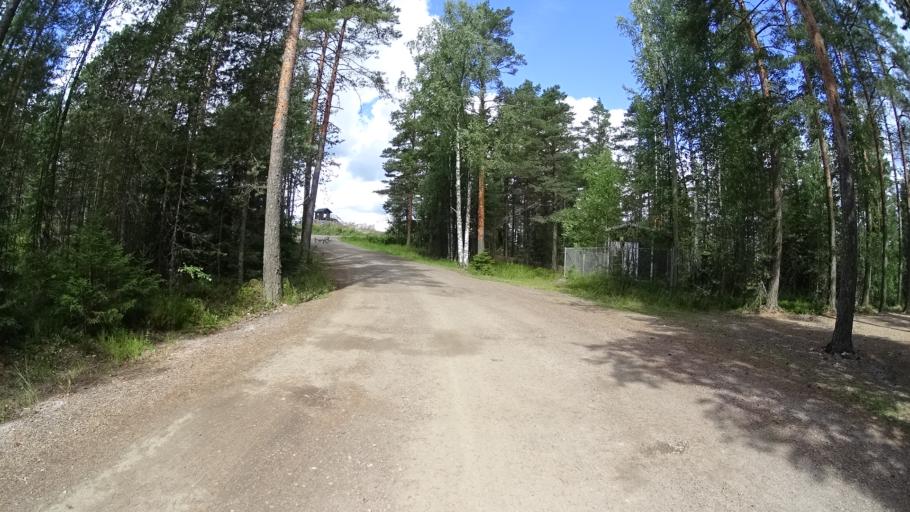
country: FI
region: Uusimaa
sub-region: Helsinki
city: Espoo
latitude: 60.2974
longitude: 24.5577
